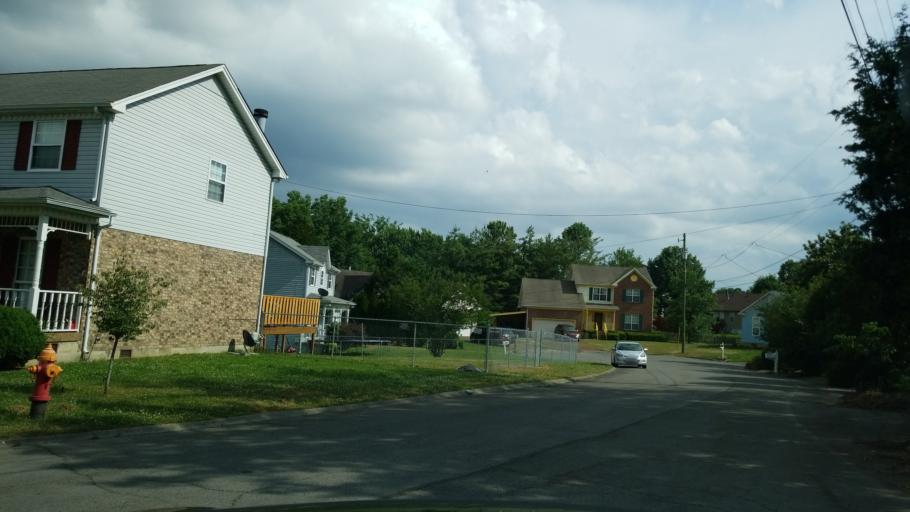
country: US
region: Tennessee
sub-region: Rutherford County
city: La Vergne
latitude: 36.0735
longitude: -86.5995
